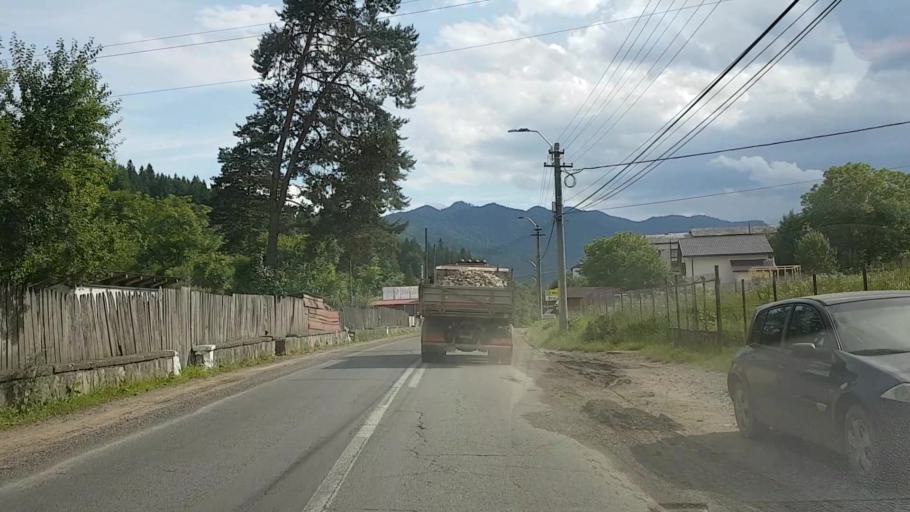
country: RO
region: Neamt
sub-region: Comuna Bicaz
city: Dodeni
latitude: 46.9284
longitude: 26.0950
